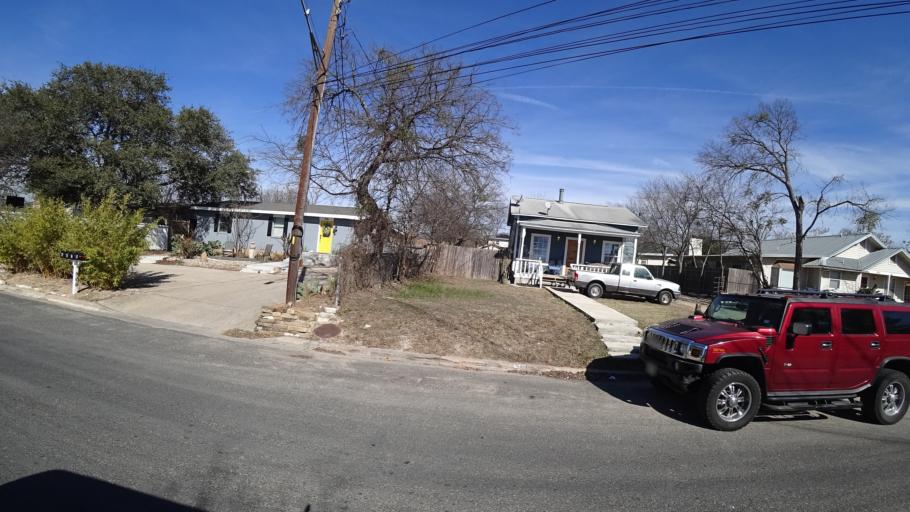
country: US
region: Texas
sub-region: Travis County
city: Wells Branch
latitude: 30.3750
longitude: -97.6878
